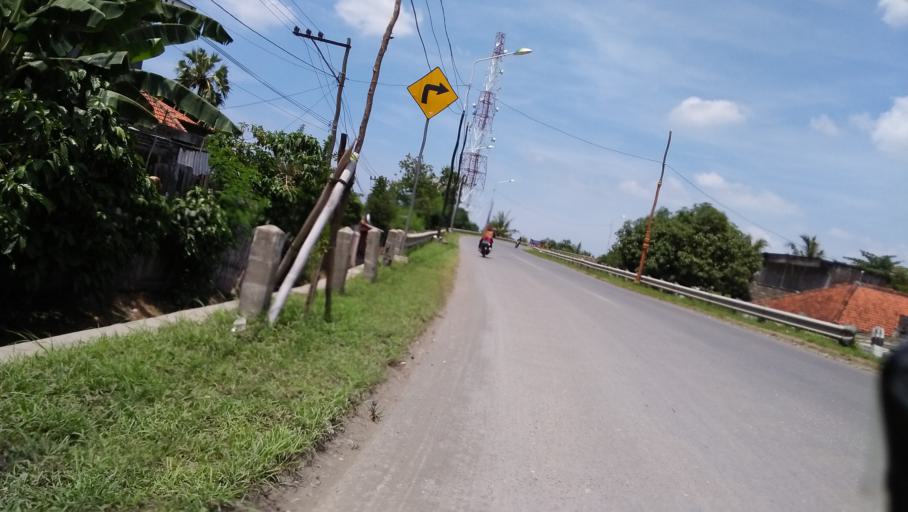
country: ID
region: Central Java
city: Semarang
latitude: -6.9855
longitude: 110.4745
